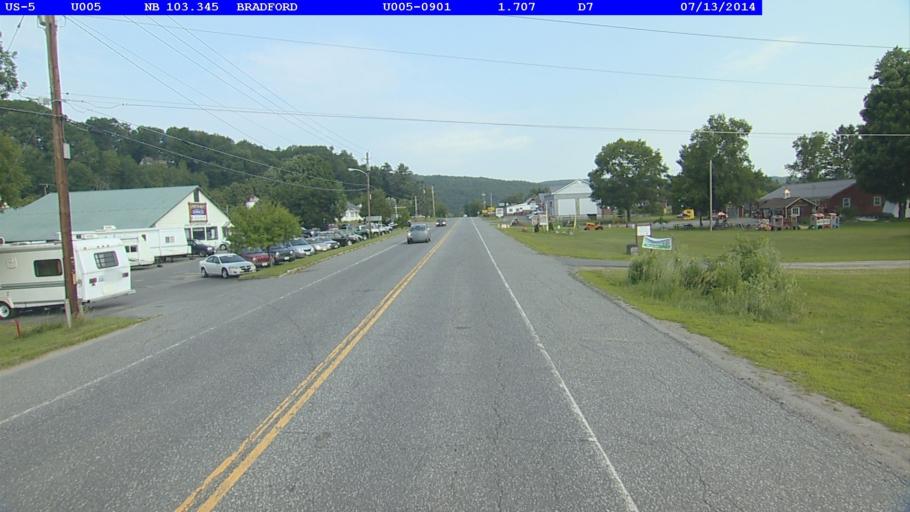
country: US
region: New Hampshire
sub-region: Grafton County
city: Haverhill
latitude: 43.9860
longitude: -72.1226
